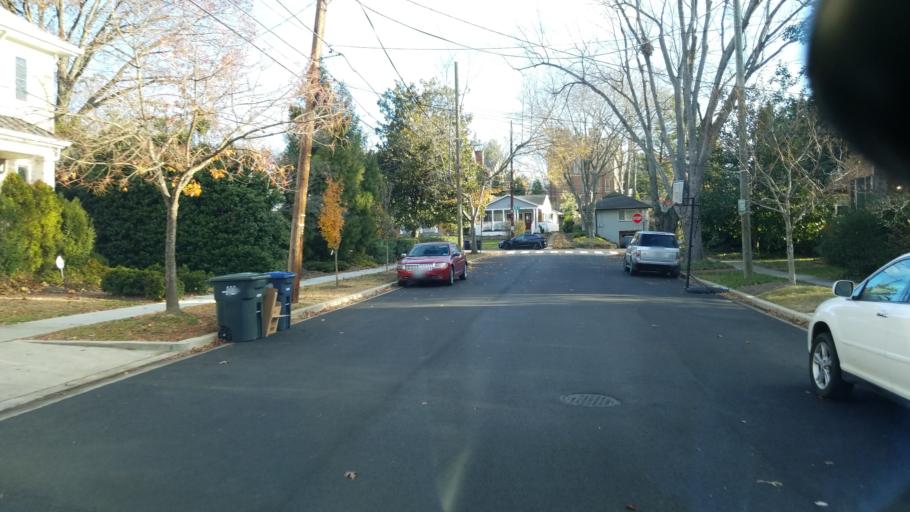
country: US
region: Virginia
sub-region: Arlington County
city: Arlington
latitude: 38.9104
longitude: -77.0862
